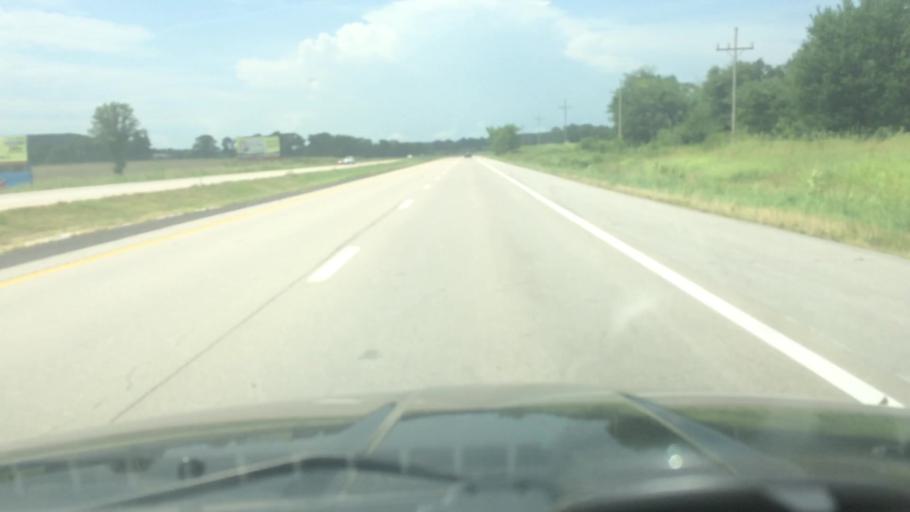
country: US
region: Missouri
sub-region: Polk County
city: Humansville
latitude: 37.8145
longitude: -93.6084
